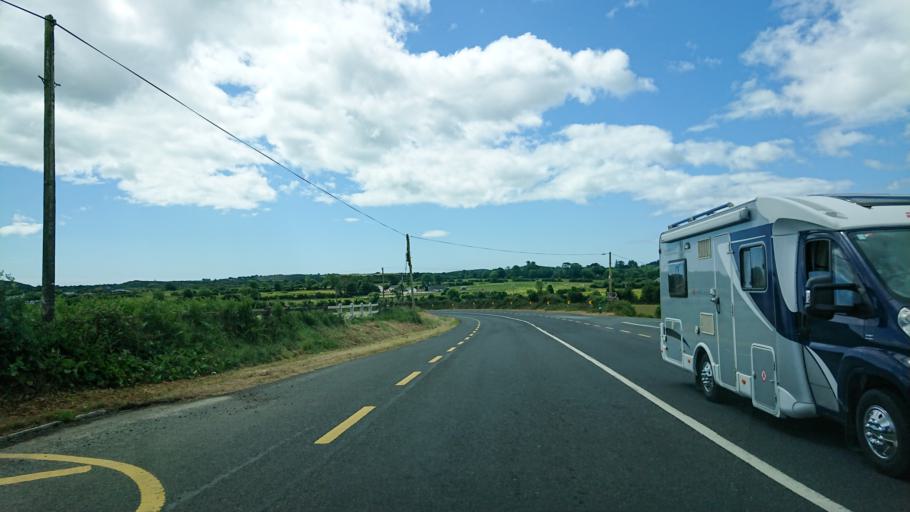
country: IE
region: Munster
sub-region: Waterford
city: Tra Mhor
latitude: 52.1980
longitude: -7.1925
